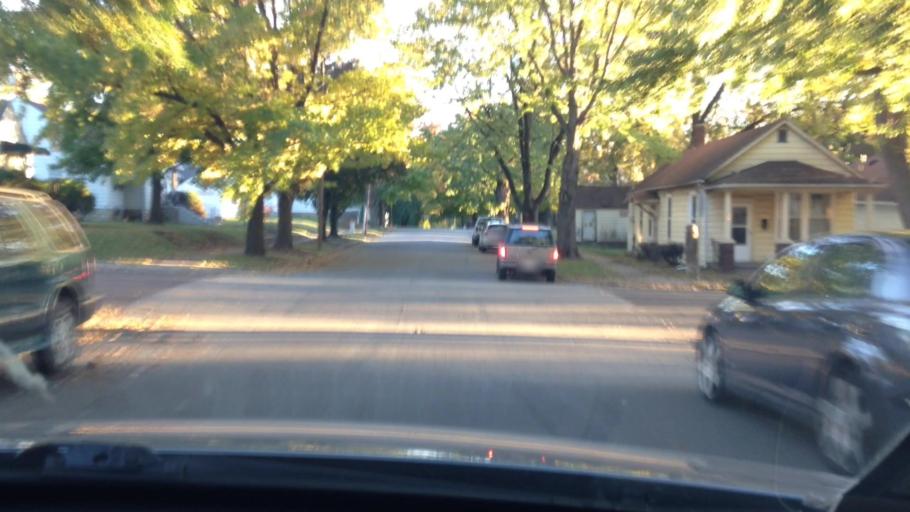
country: US
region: Kansas
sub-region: Leavenworth County
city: Leavenworth
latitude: 39.3250
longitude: -94.9185
